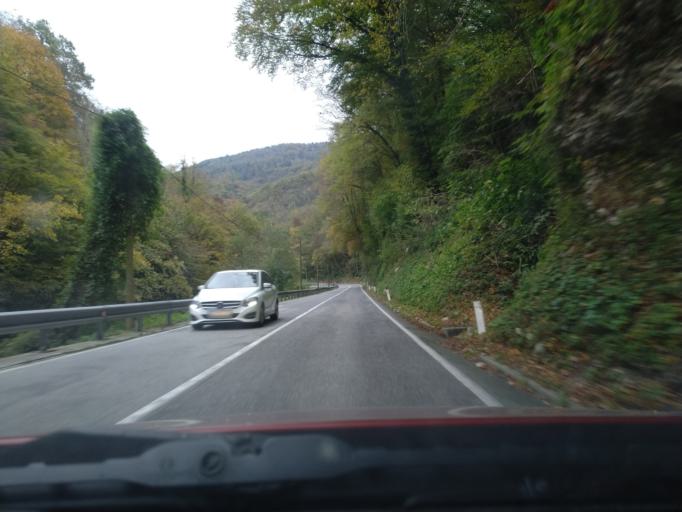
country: SI
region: Tolmin
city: Tolmin
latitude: 46.1381
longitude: 13.7157
